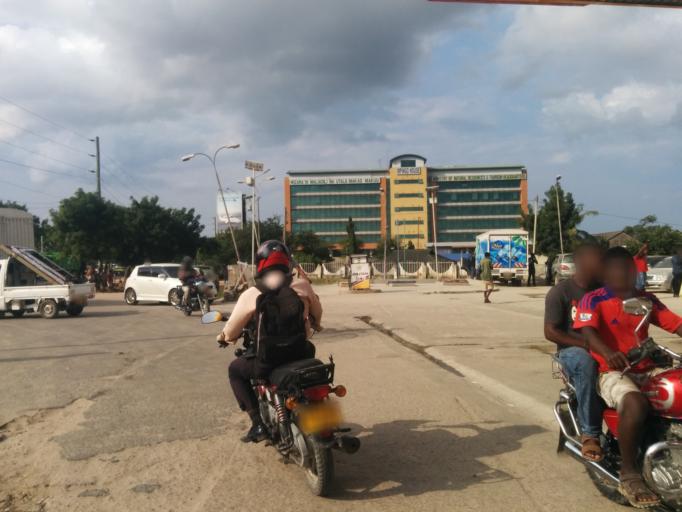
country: TZ
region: Dar es Salaam
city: Dar es Salaam
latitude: -6.8320
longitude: 39.2694
